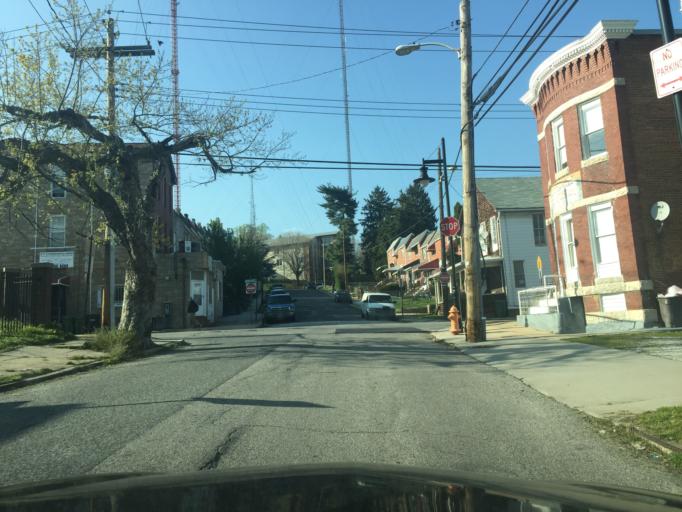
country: US
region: Maryland
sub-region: City of Baltimore
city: Baltimore
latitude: 39.3317
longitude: -76.6484
